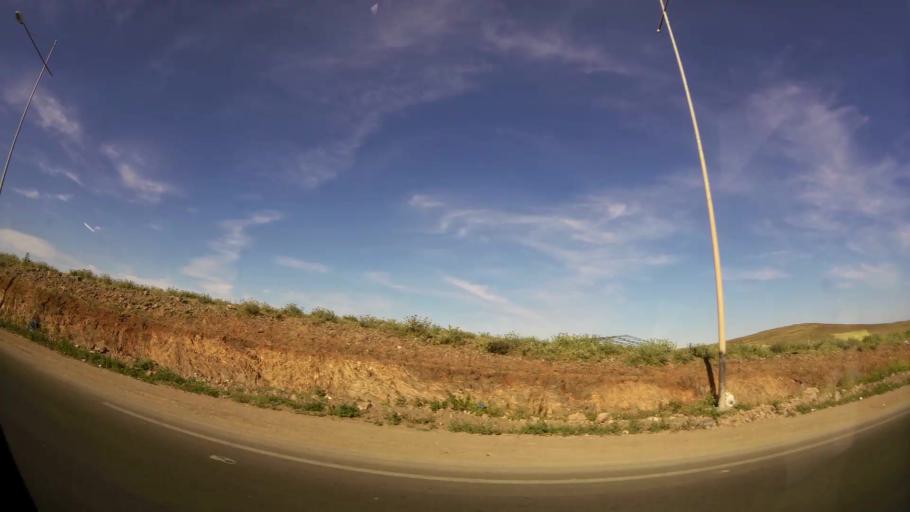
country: MA
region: Marrakech-Tensift-Al Haouz
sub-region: Marrakech
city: Marrakesh
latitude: 31.7071
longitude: -8.0644
